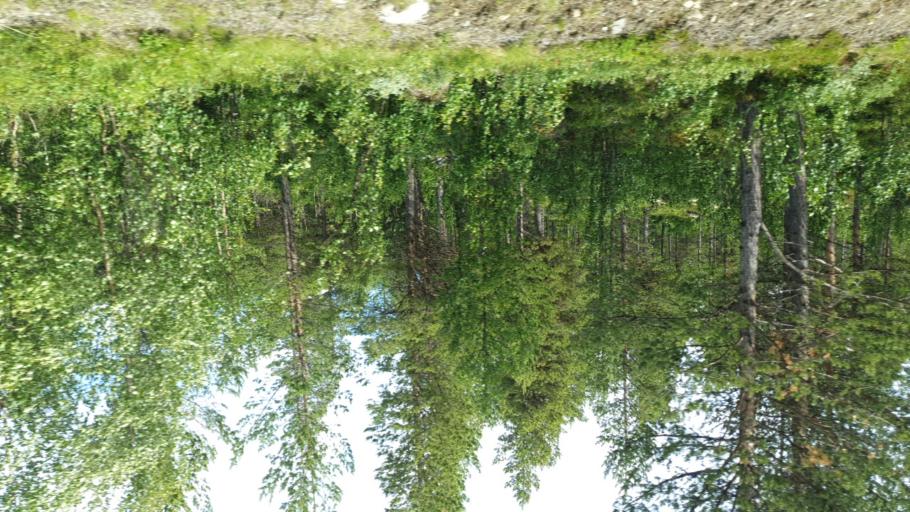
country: NO
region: Oppland
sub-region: Vaga
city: Vagamo
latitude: 61.6930
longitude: 9.0597
